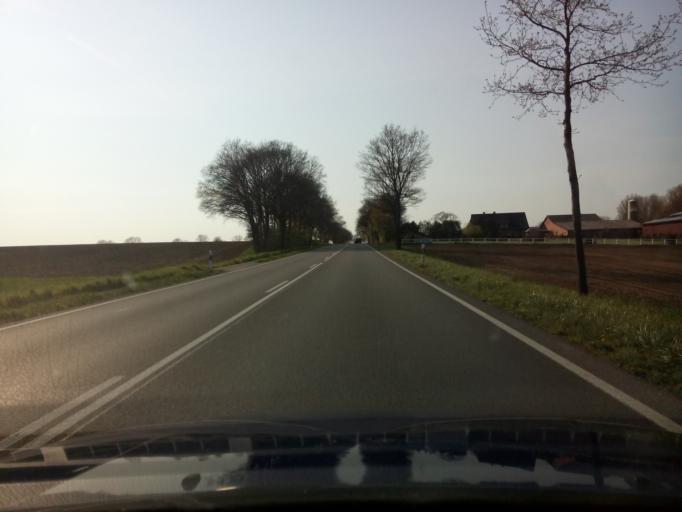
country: DE
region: Lower Saxony
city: Sustedt
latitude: 52.8361
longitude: 8.9131
